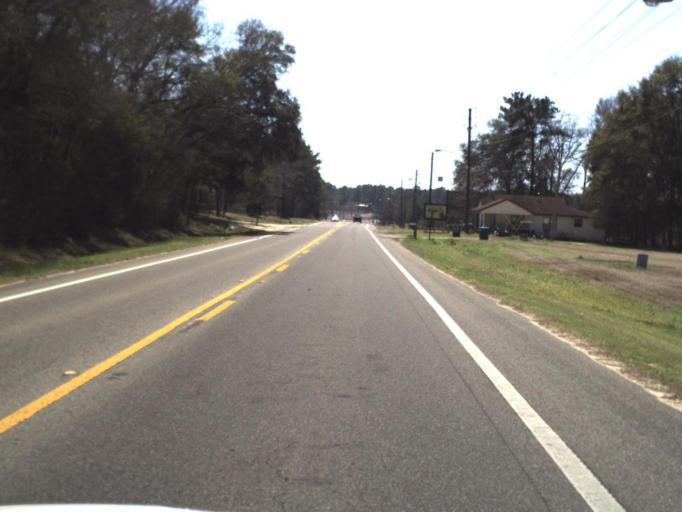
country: US
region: Florida
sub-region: Jackson County
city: Marianna
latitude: 30.7708
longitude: -85.2545
